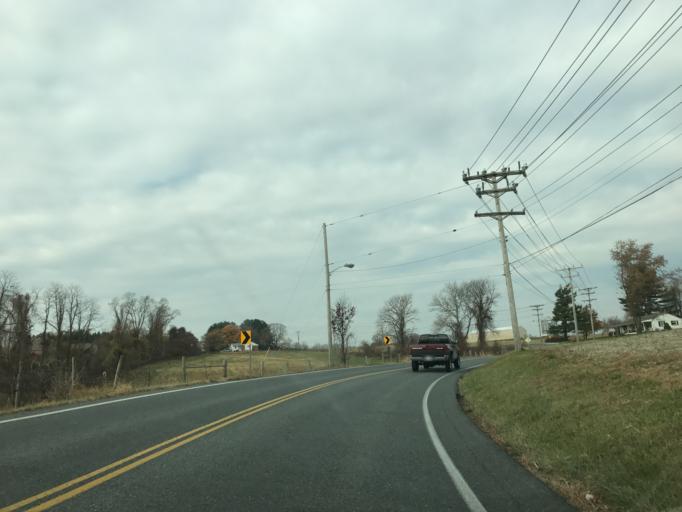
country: US
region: Maryland
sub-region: Harford County
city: Bel Air North
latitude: 39.5799
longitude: -76.4167
